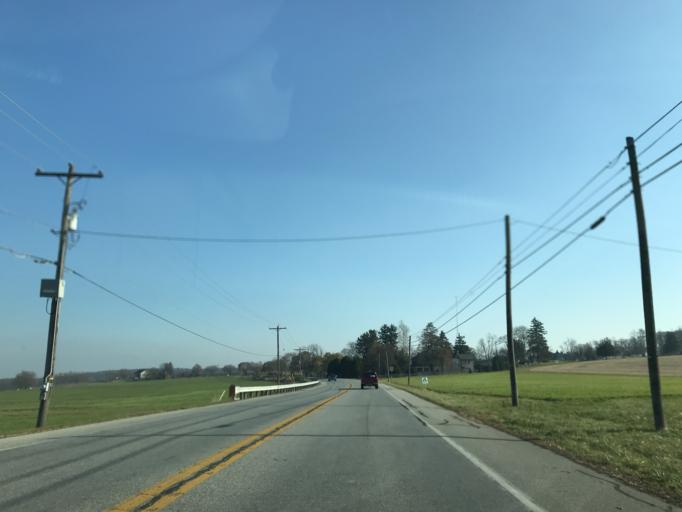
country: US
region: Pennsylvania
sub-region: Adams County
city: Mount Pleasant
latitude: 39.7537
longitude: -77.0576
